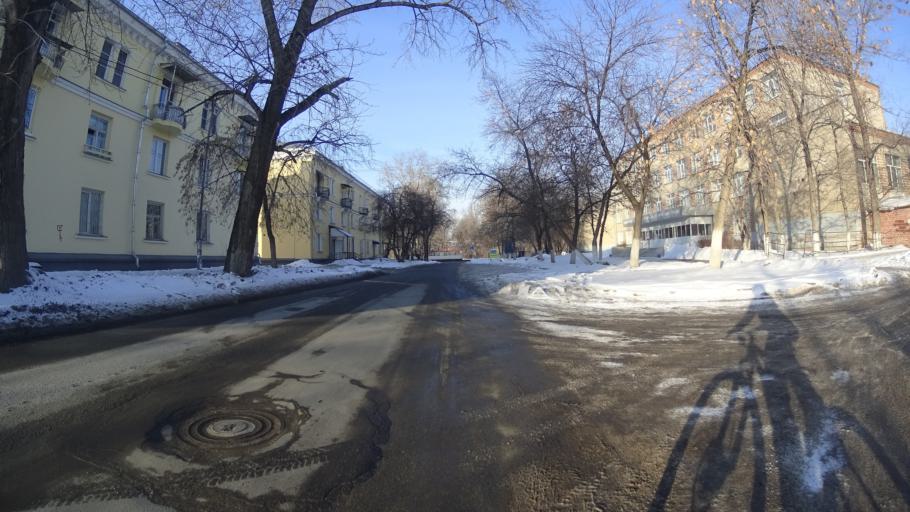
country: RU
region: Chelyabinsk
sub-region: Gorod Chelyabinsk
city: Chelyabinsk
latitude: 55.1669
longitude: 61.4385
